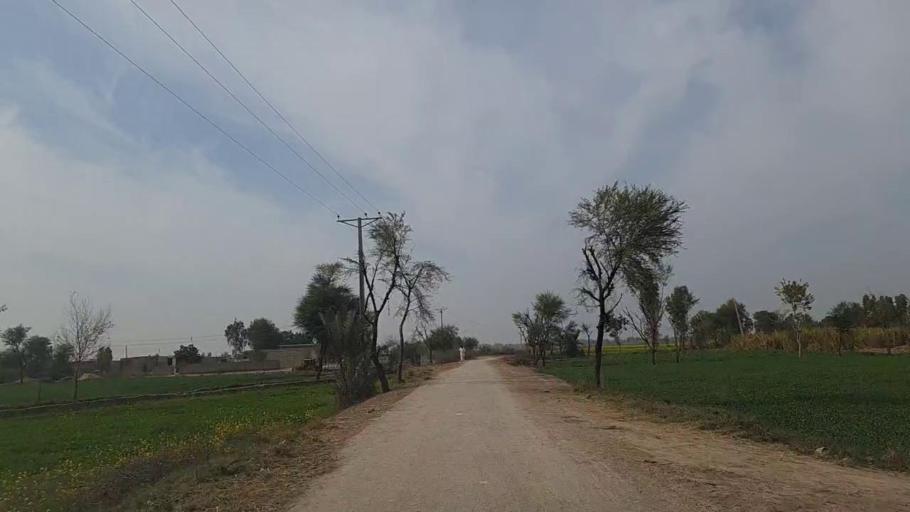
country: PK
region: Sindh
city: Daur
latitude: 26.4505
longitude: 68.4160
